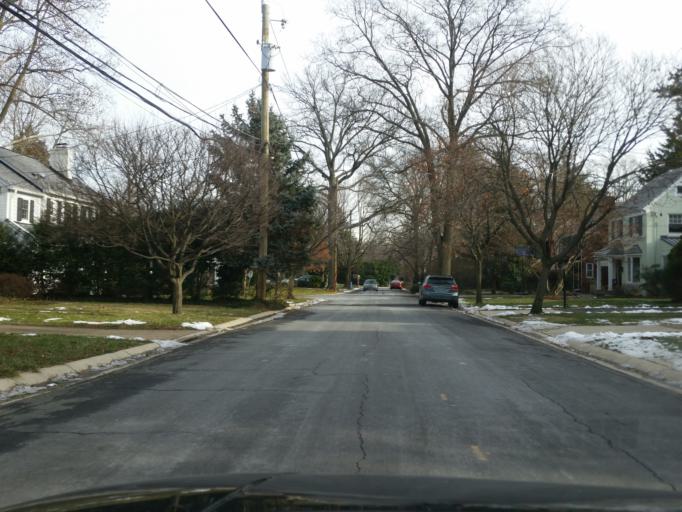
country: US
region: Maryland
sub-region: Montgomery County
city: Chevy Chase
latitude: 38.9805
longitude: -77.0631
